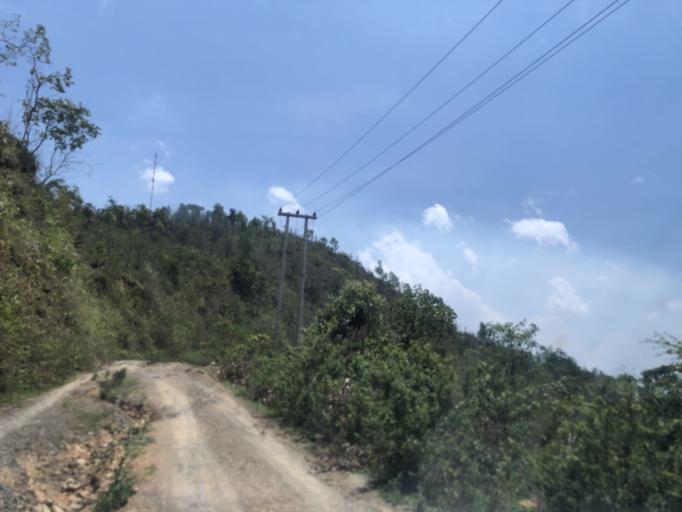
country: LA
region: Phongsali
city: Phongsali
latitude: 21.4388
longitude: 102.1619
